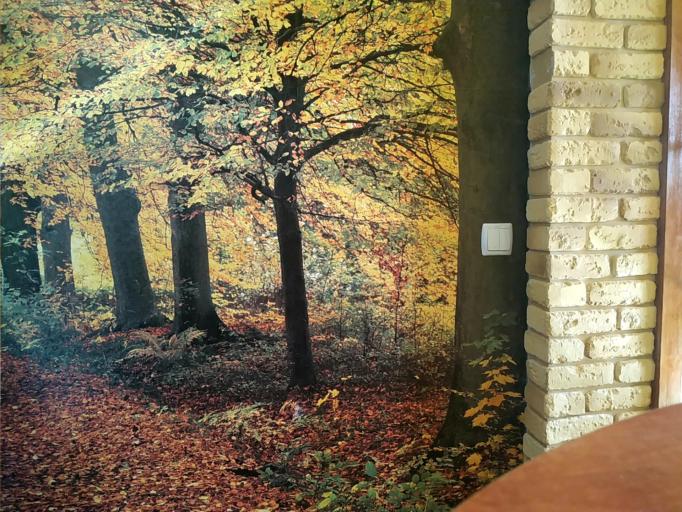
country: RU
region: Jaroslavl
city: Kukoboy
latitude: 58.8146
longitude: 39.7696
